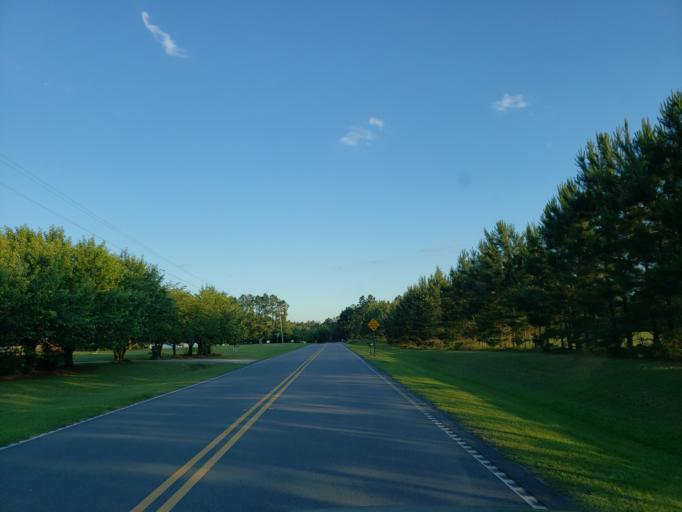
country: US
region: Georgia
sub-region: Lowndes County
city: Valdosta
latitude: 30.7357
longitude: -83.2504
